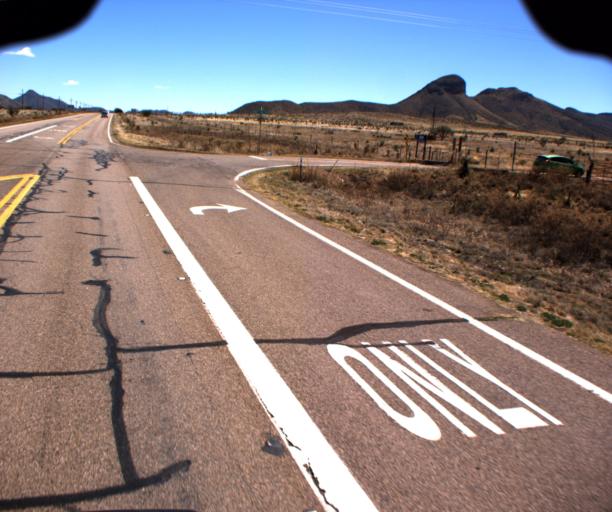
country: US
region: Arizona
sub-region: Cochise County
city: Huachuca City
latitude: 31.7239
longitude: -110.5249
